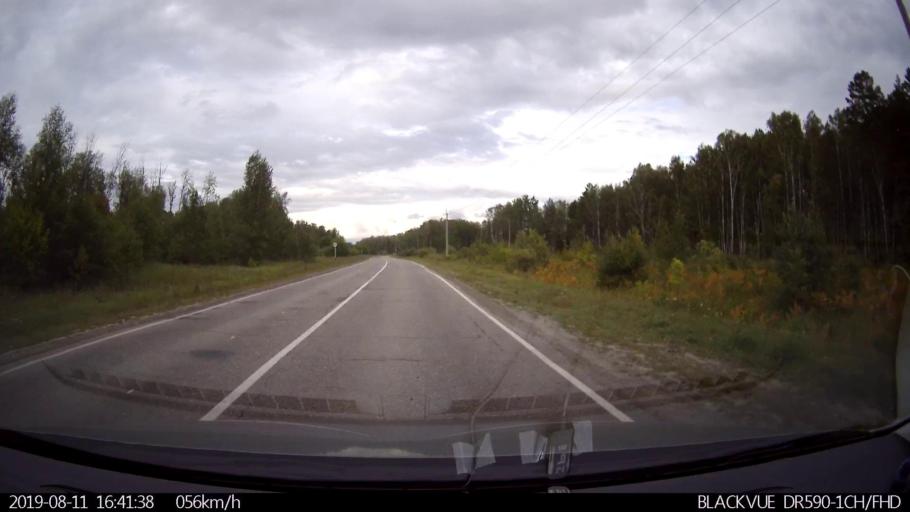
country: RU
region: Ulyanovsk
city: Mayna
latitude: 54.1547
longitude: 47.6545
